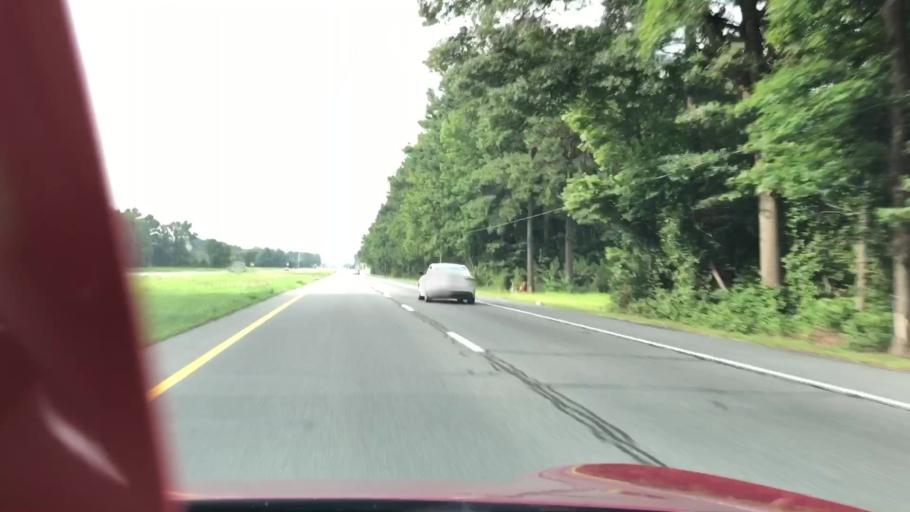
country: US
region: Delaware
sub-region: Kent County
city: Harrington
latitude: 38.9012
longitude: -75.5710
